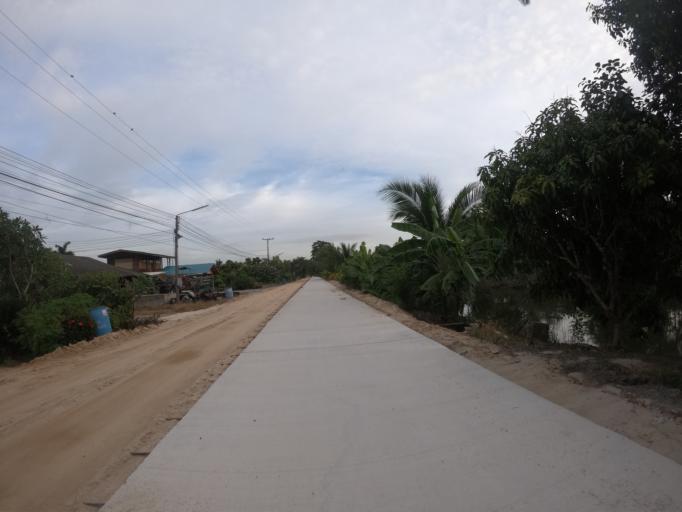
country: TH
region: Pathum Thani
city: Ban Rangsit
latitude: 14.0168
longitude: 100.7996
